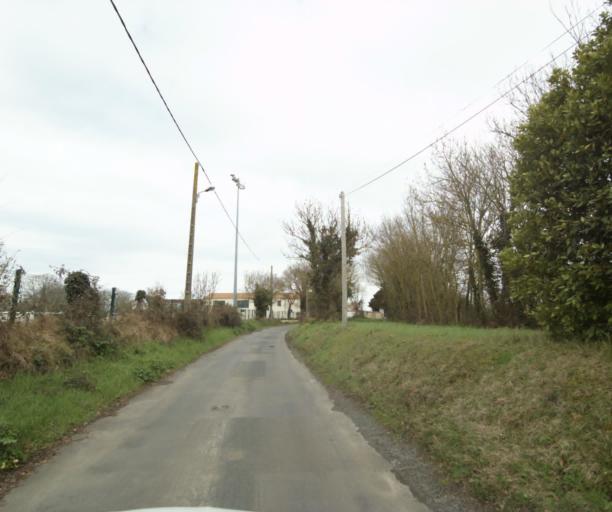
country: FR
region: Poitou-Charentes
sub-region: Departement de la Charente-Maritime
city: Lagord
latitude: 46.1899
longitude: -1.1673
